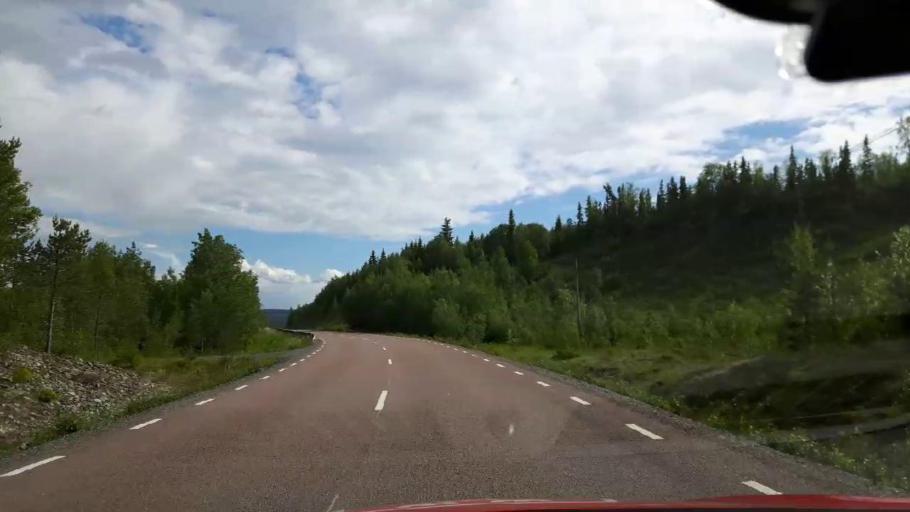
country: SE
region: Jaemtland
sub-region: Krokoms Kommun
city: Valla
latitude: 63.9279
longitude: 14.2111
